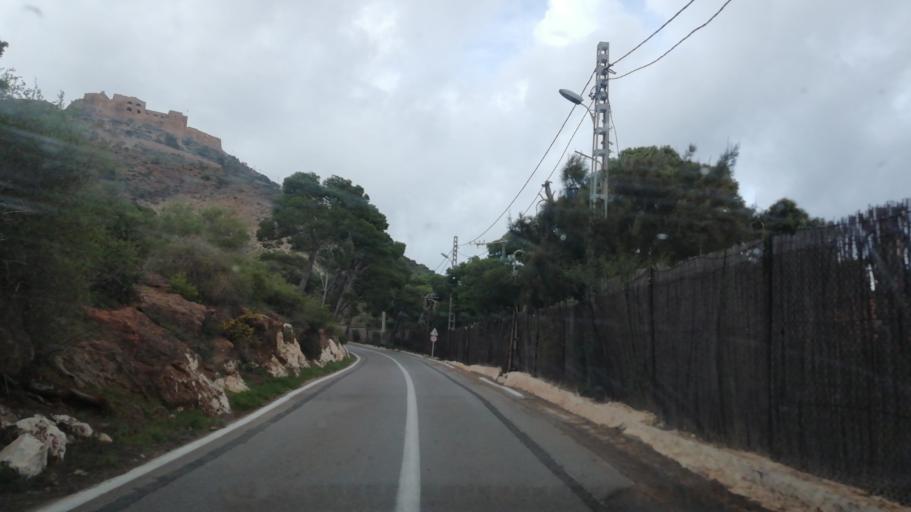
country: DZ
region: Oran
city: Oran
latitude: 35.7036
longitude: -0.6620
